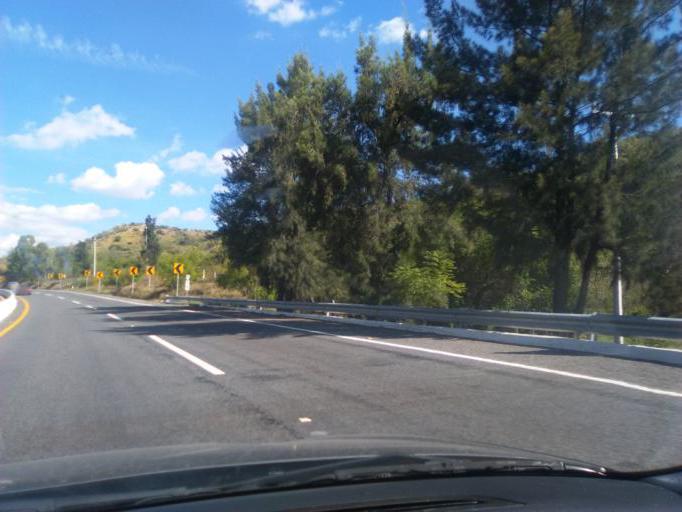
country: MX
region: Guanajuato
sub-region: Silao de la Victoria
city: Aguas Buenas
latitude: 20.9585
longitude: -101.3507
